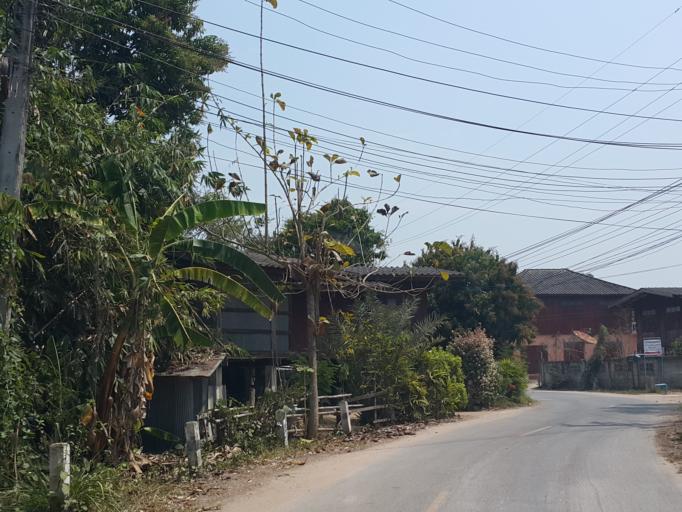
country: TH
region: Lampang
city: Mueang Pan
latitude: 18.7836
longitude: 99.5166
